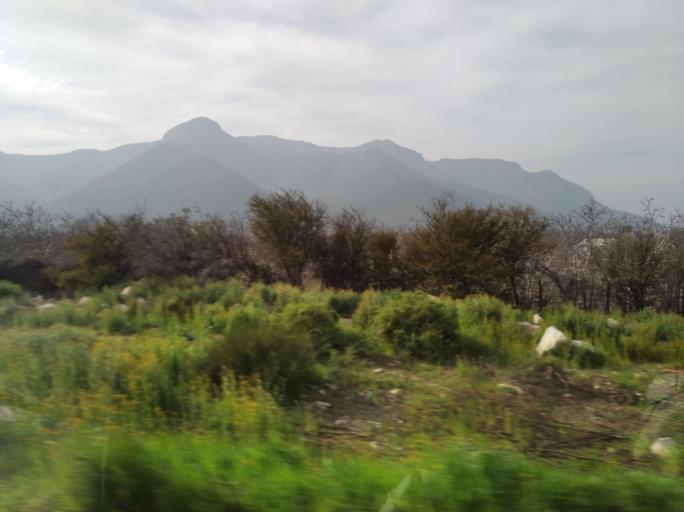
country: CL
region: Santiago Metropolitan
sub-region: Provincia de Chacabuco
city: Lampa
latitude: -33.2207
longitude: -70.9225
